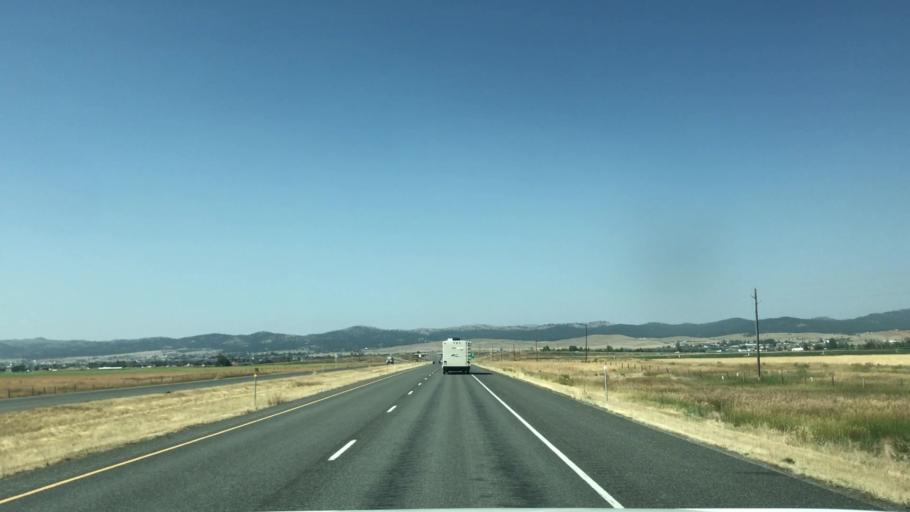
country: US
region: Montana
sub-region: Lewis and Clark County
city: Helena Valley West Central
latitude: 46.6952
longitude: -112.0117
